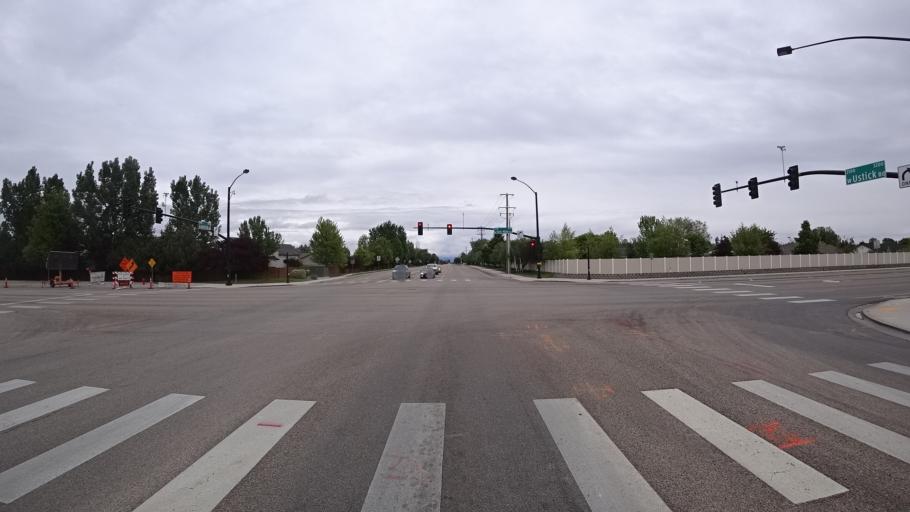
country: US
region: Idaho
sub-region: Ada County
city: Meridian
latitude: 43.6340
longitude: -116.4339
